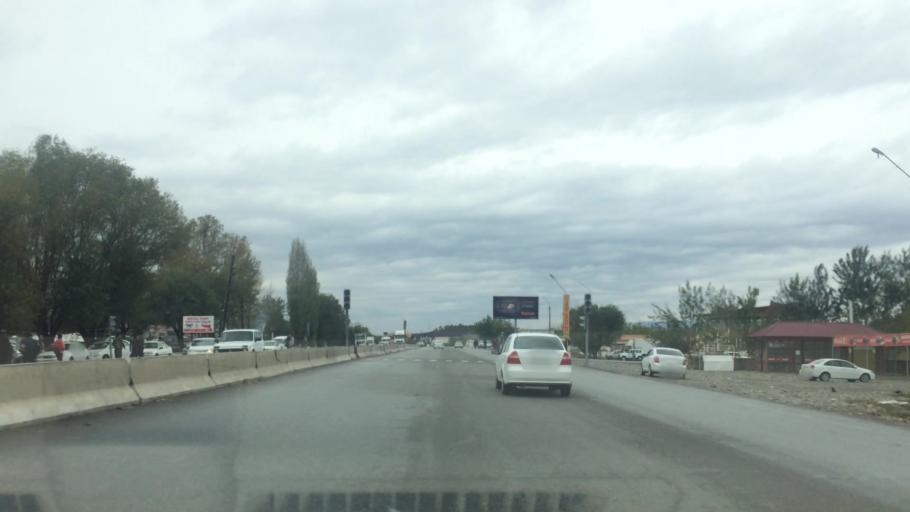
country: UZ
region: Jizzax
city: Jizzax
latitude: 40.0125
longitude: 67.6021
